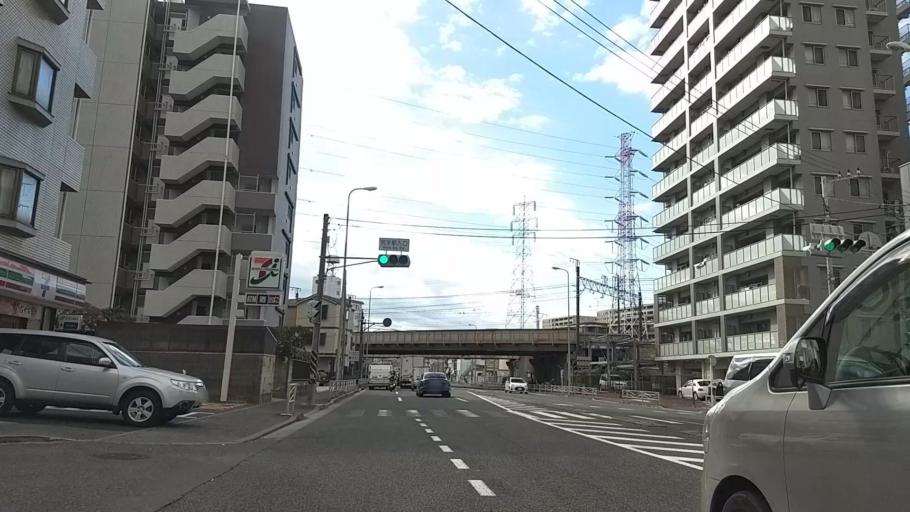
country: JP
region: Kanagawa
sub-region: Kawasaki-shi
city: Kawasaki
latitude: 35.5305
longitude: 139.6854
